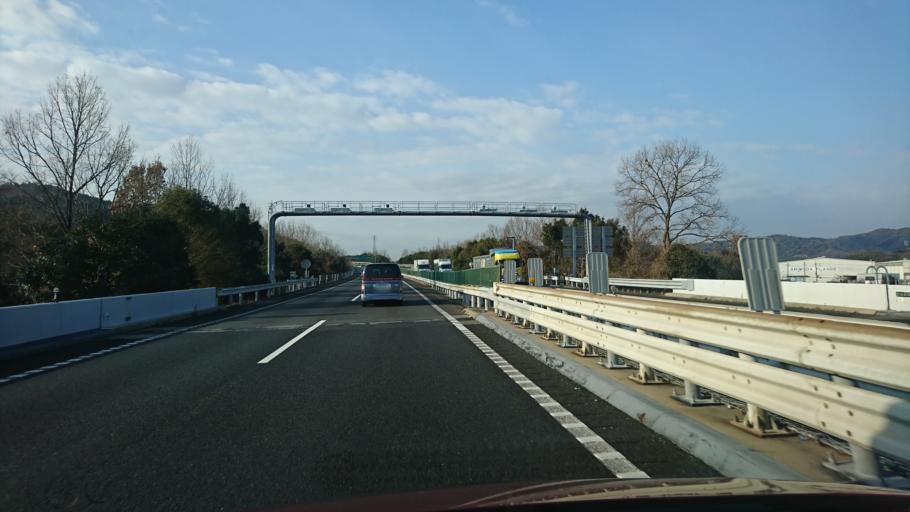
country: JP
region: Hyogo
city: Tatsunocho-tominaga
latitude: 34.8436
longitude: 134.5172
